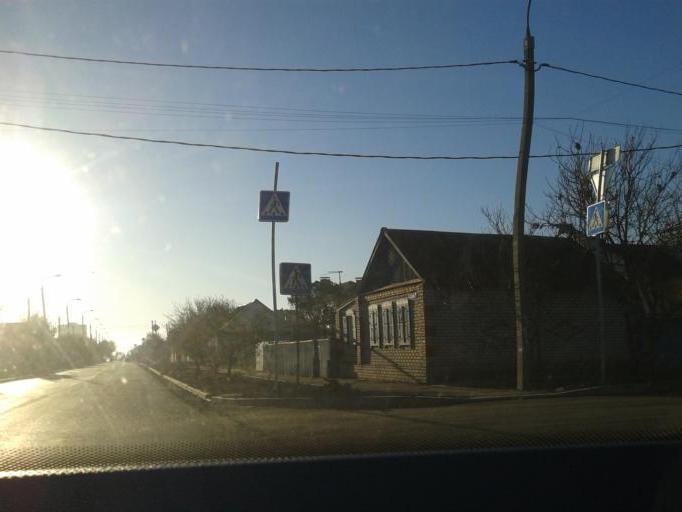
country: RU
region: Volgograd
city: Volgograd
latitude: 48.6992
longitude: 44.4649
